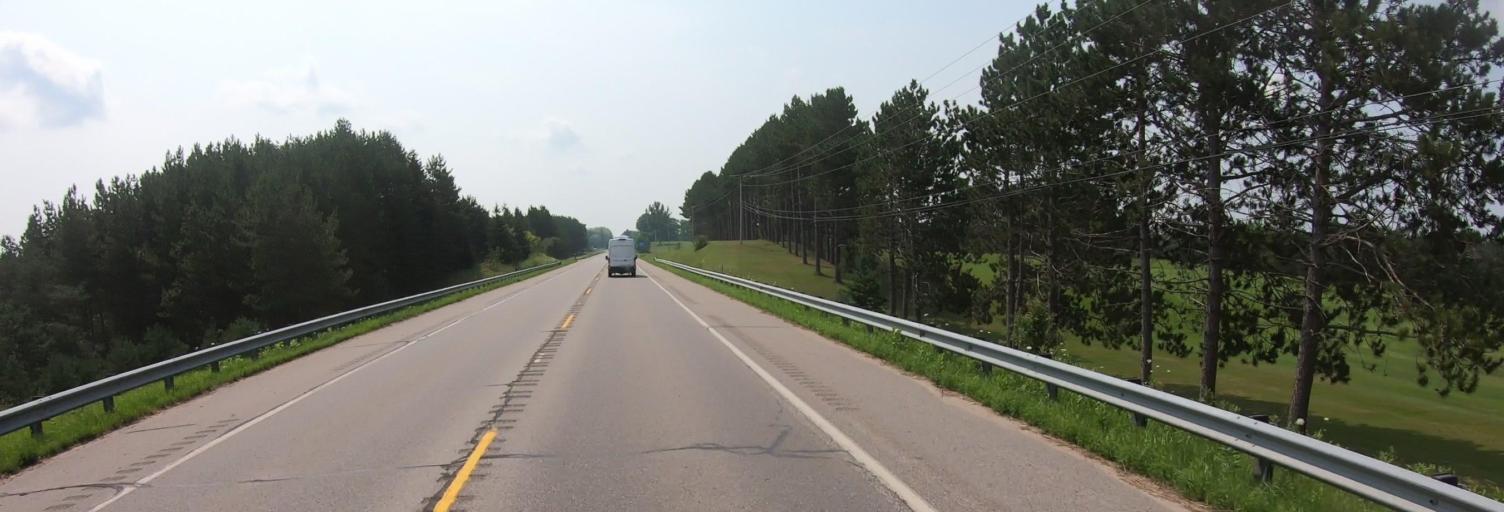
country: US
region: Michigan
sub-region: Luce County
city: Newberry
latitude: 46.3100
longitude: -85.5096
